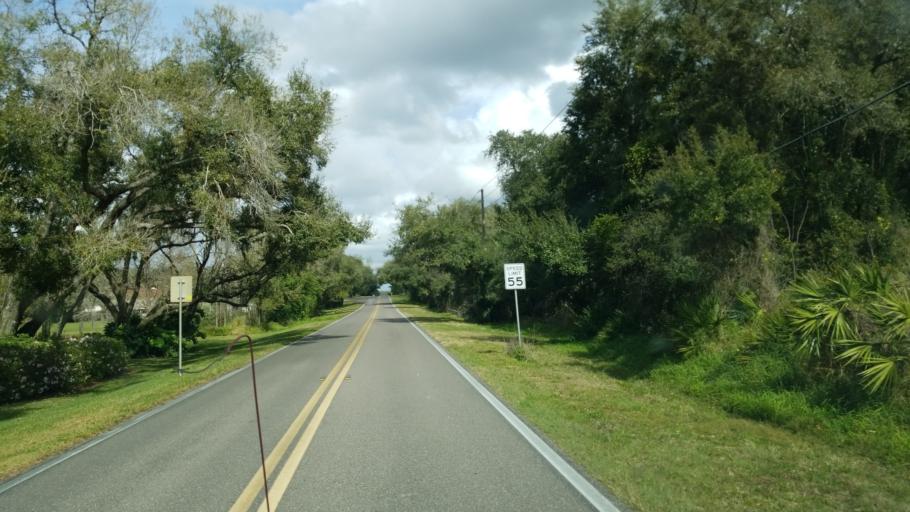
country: US
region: Florida
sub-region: Polk County
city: Dundee
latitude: 28.0604
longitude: -81.5543
